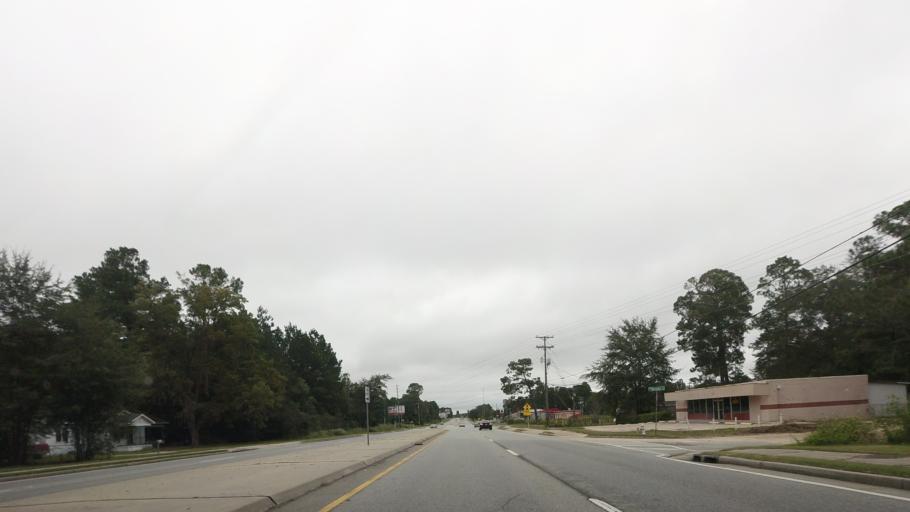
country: US
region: Georgia
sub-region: Lowndes County
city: Valdosta
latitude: 30.9386
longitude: -83.2395
